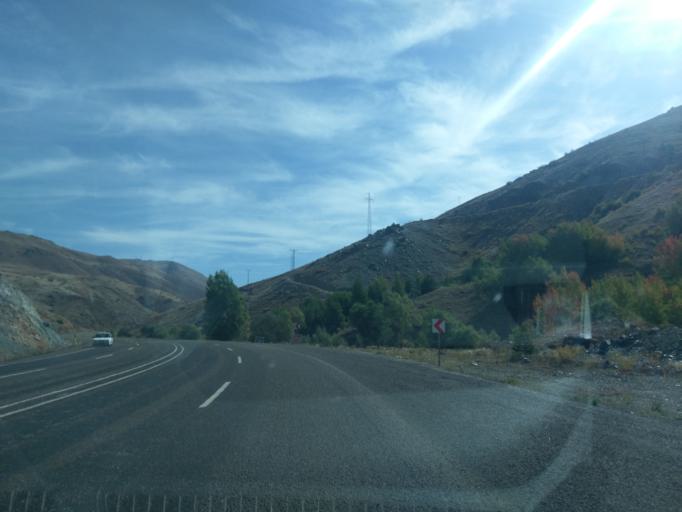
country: TR
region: Sivas
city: Imranli
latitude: 39.8597
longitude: 38.3215
